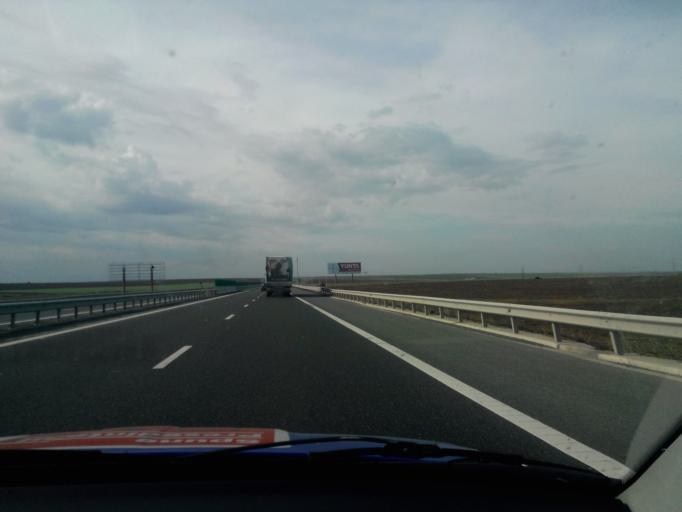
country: RO
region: Constanta
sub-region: Comuna Cumpana
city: Cumpana
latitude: 44.1440
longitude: 28.5391
